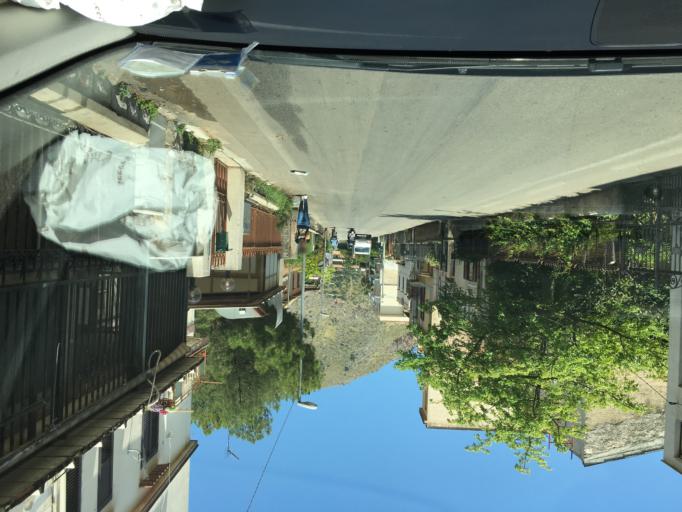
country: IT
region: Sicily
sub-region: Palermo
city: Palermo
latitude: 38.1985
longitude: 13.3185
